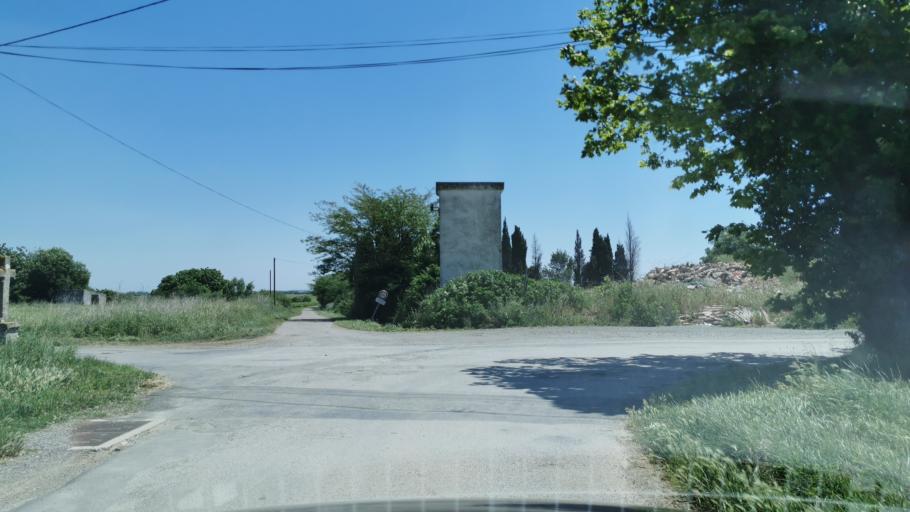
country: FR
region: Languedoc-Roussillon
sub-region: Departement de l'Aude
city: Saint-Marcel-sur-Aude
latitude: 43.2625
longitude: 2.9573
